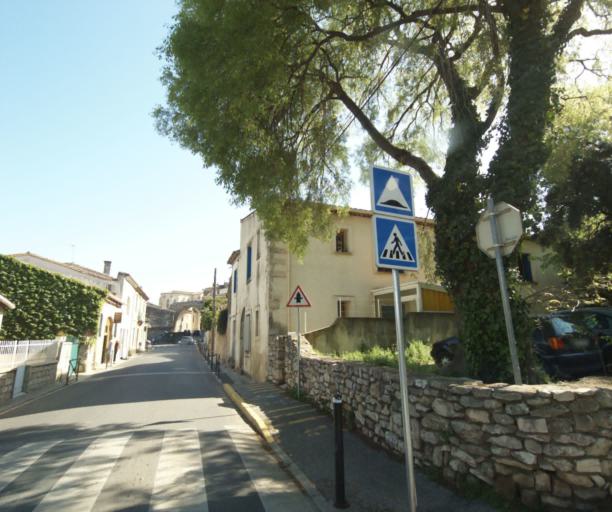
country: FR
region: Languedoc-Roussillon
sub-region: Departement de l'Herault
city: Castries
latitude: 43.6798
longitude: 3.9857
